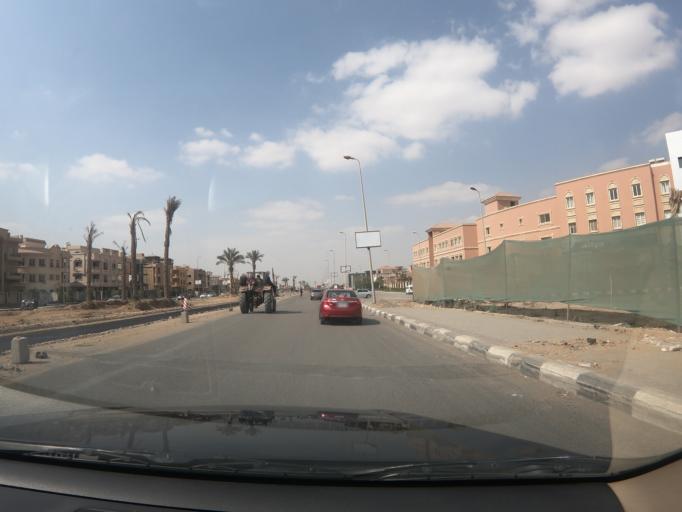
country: EG
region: Muhafazat al Qalyubiyah
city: Al Khankah
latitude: 30.0454
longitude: 31.4751
